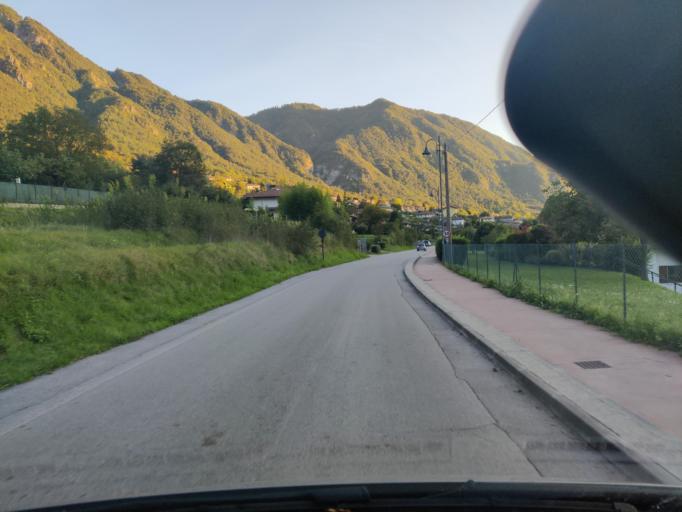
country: IT
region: Lombardy
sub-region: Provincia di Brescia
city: Crone
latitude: 45.7463
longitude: 10.4853
